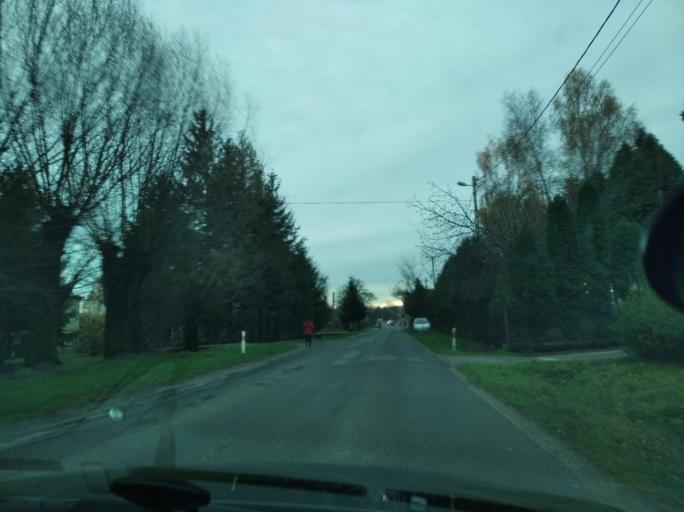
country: PL
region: Subcarpathian Voivodeship
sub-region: Powiat lancucki
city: Krzemienica
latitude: 50.0843
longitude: 22.1880
